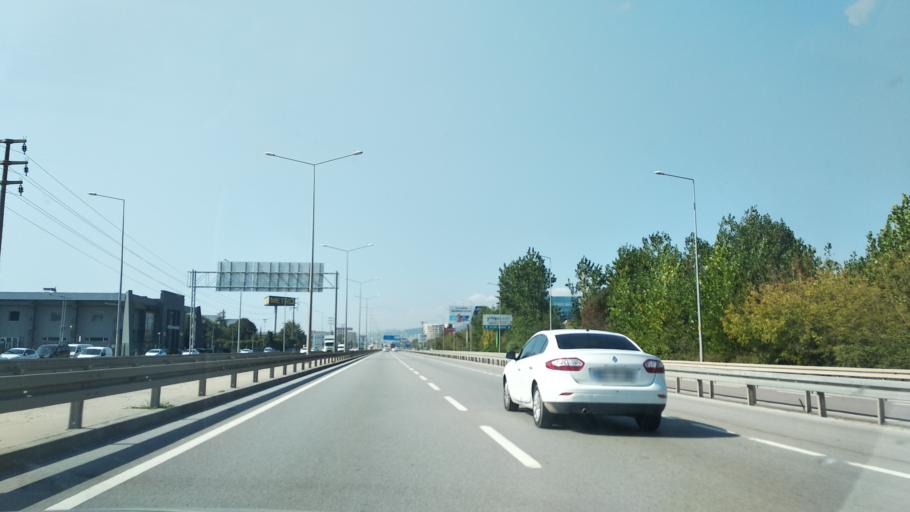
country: TR
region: Kocaeli
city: Kosekoy
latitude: 40.7570
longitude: 29.9990
